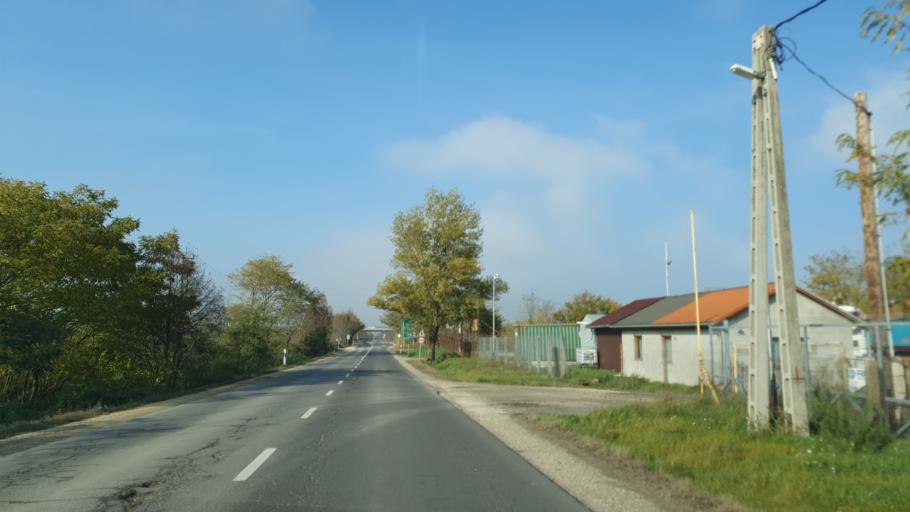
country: HU
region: Pest
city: Szod
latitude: 47.7434
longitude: 19.1812
